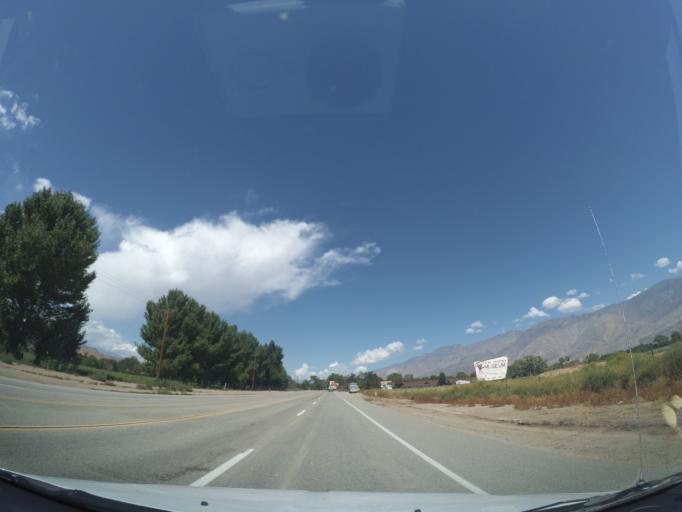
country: US
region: California
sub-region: Inyo County
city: Lone Pine
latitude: 36.5913
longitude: -118.0576
